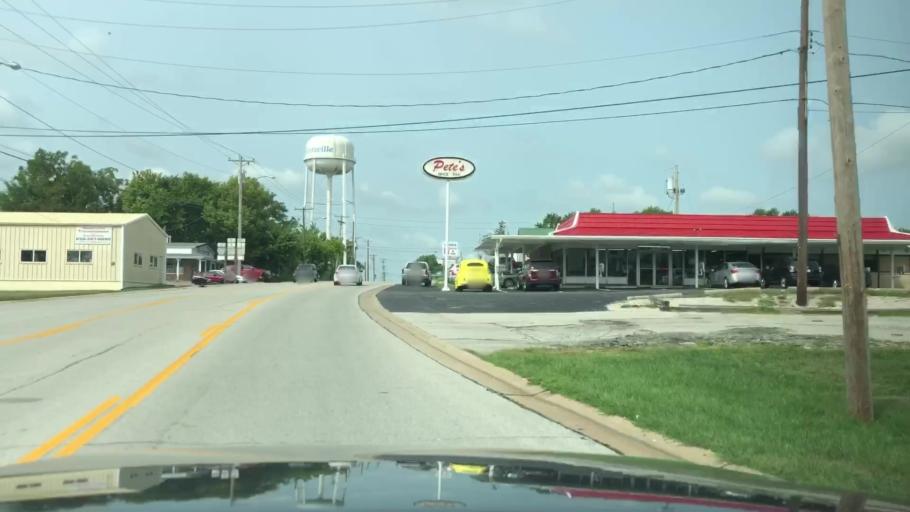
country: US
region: Missouri
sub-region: Saint Charles County
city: Wentzville
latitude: 38.8136
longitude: -90.8445
